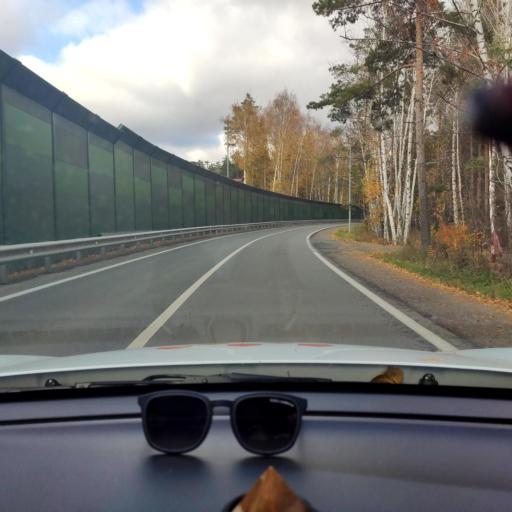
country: RU
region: Tatarstan
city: Verkhniy Uslon
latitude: 55.6281
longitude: 49.0141
